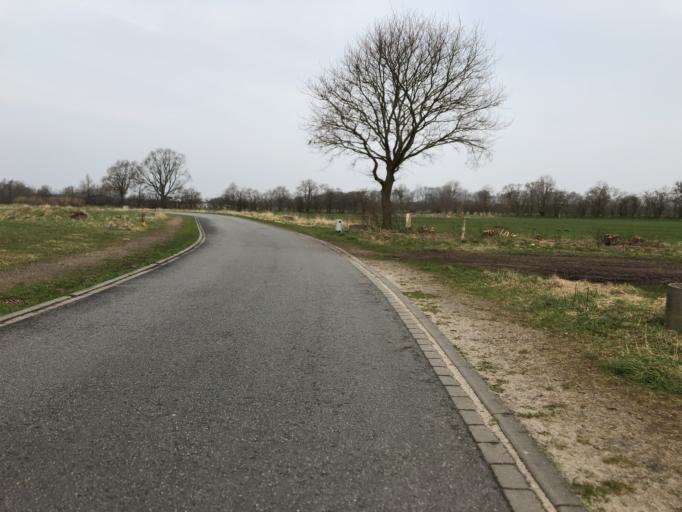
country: DE
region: Schleswig-Holstein
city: Wanderup
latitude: 54.6942
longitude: 9.3422
